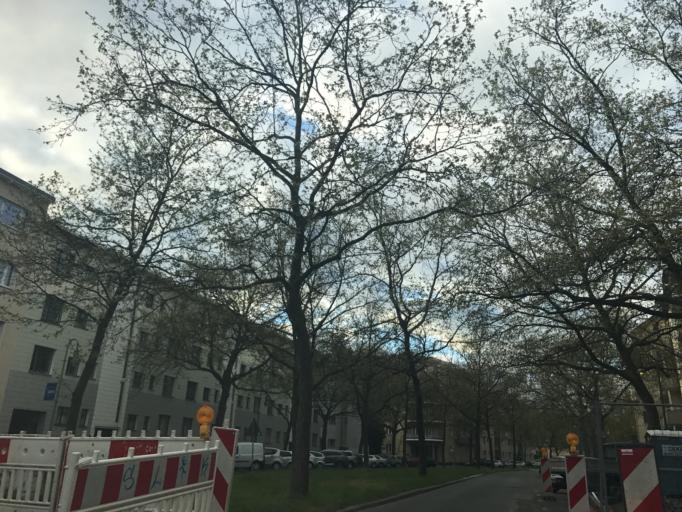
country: DE
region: Berlin
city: Westend
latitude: 52.5169
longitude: 13.2612
